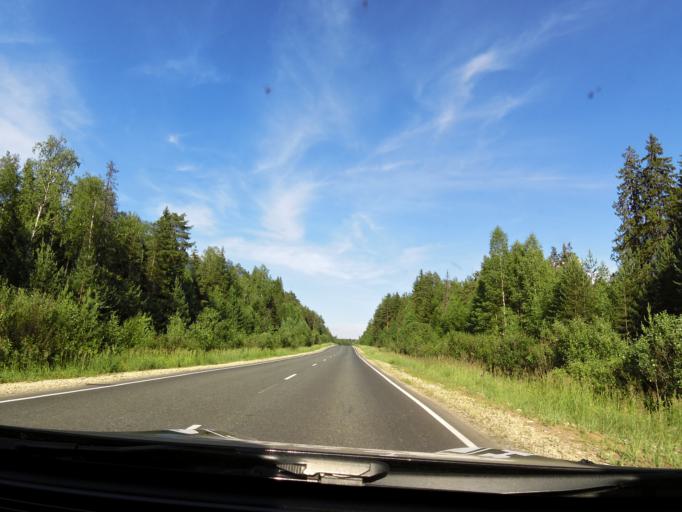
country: RU
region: Kirov
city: Dubrovka
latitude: 58.9071
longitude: 51.2348
